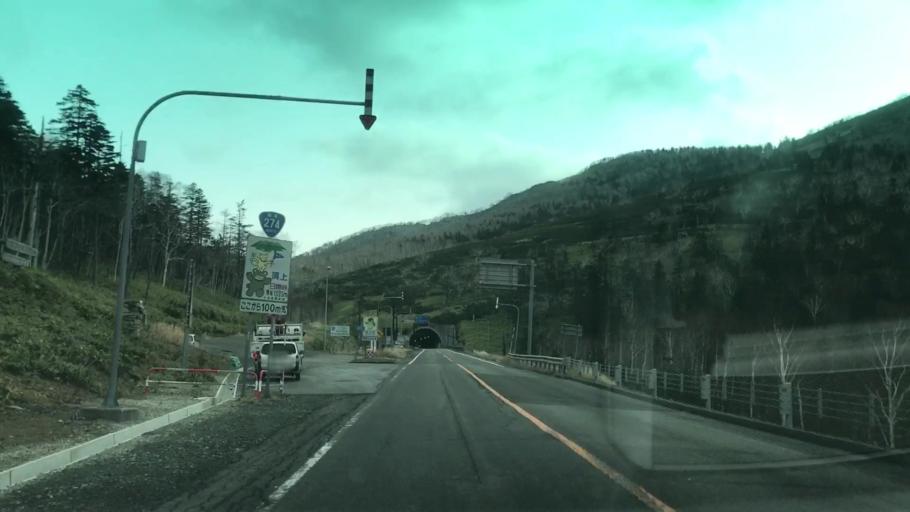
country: JP
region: Hokkaido
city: Otofuke
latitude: 42.9769
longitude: 142.7460
